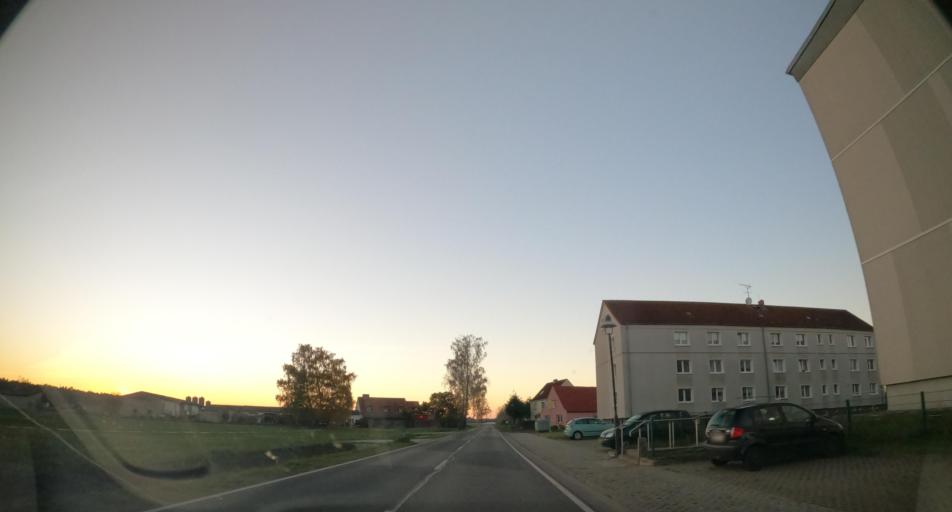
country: DE
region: Mecklenburg-Vorpommern
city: Ducherow
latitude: 53.7769
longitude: 13.8862
